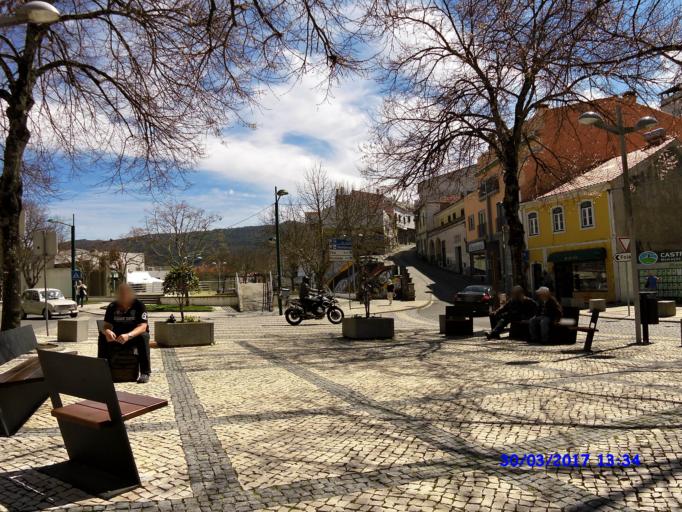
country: PT
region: Faro
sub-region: Monchique
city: Monchique
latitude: 37.3180
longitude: -8.5566
